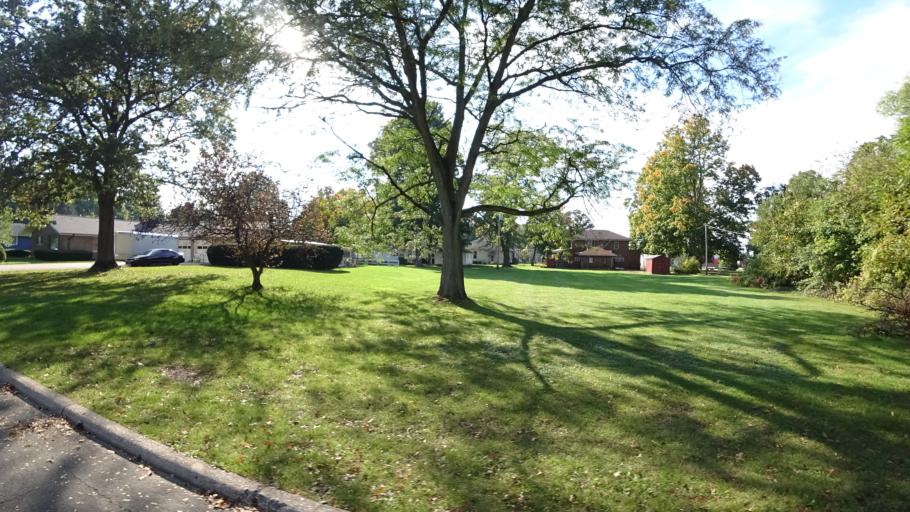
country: US
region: Michigan
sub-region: Saint Joseph County
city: Three Rivers
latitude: 41.9581
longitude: -85.6333
